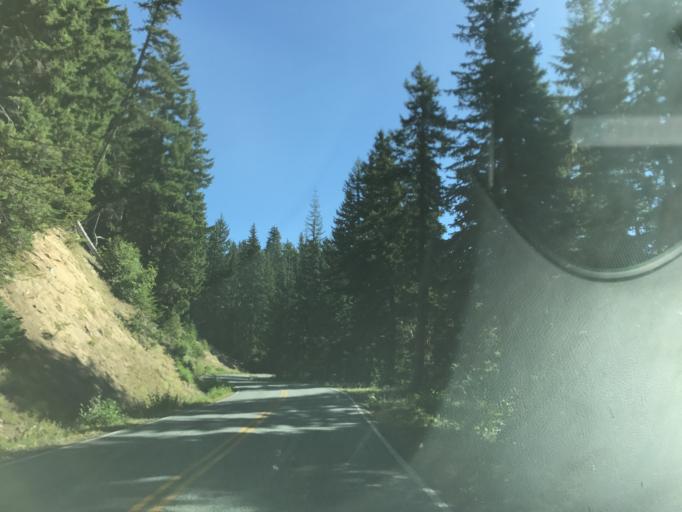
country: US
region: Washington
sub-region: King County
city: Enumclaw
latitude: 46.9118
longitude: -121.5812
